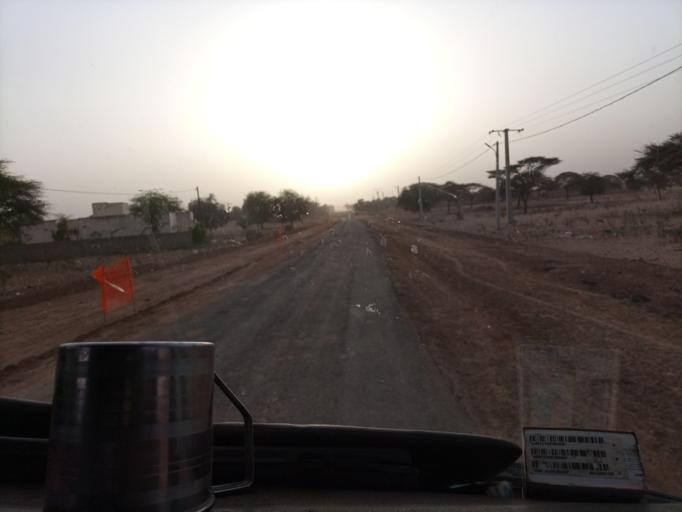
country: SN
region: Louga
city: Dara
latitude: 15.4023
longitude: -15.6581
